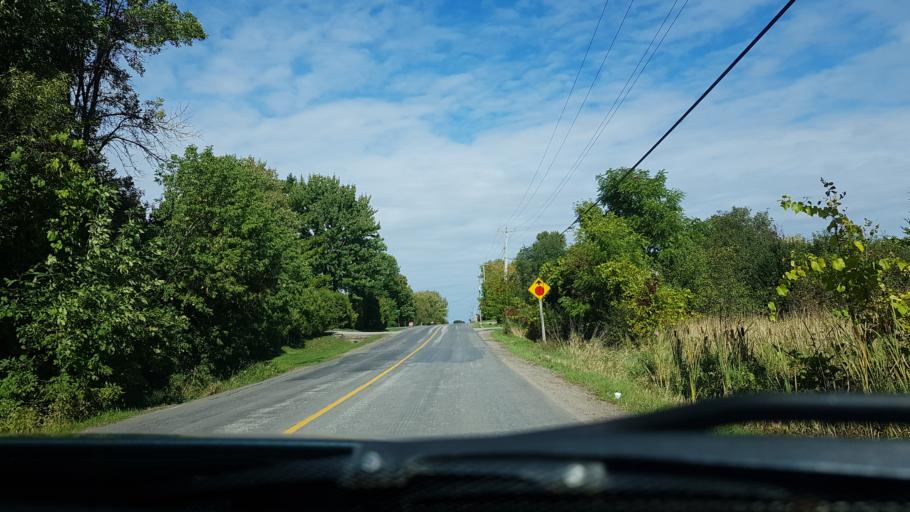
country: CA
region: Ontario
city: Orillia
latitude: 44.5959
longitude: -79.3188
